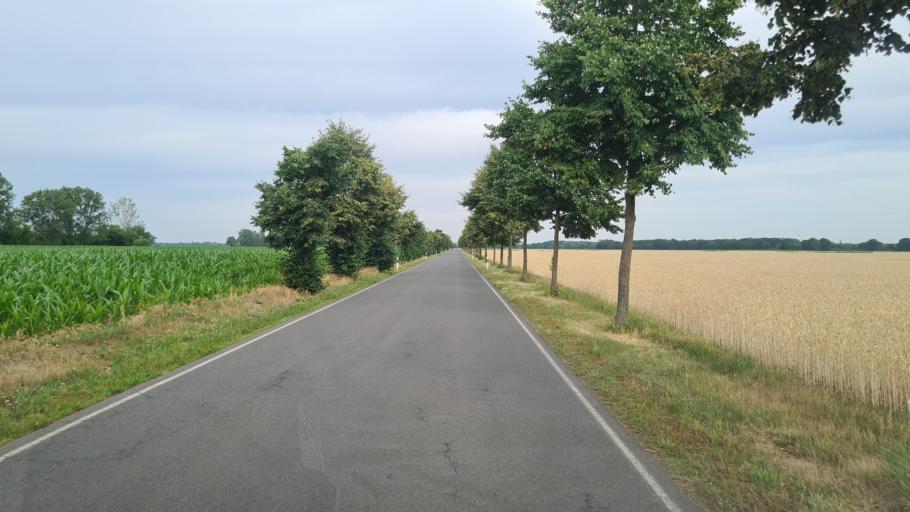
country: DE
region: Saxony-Anhalt
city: Jessen
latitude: 51.7835
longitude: 12.9163
